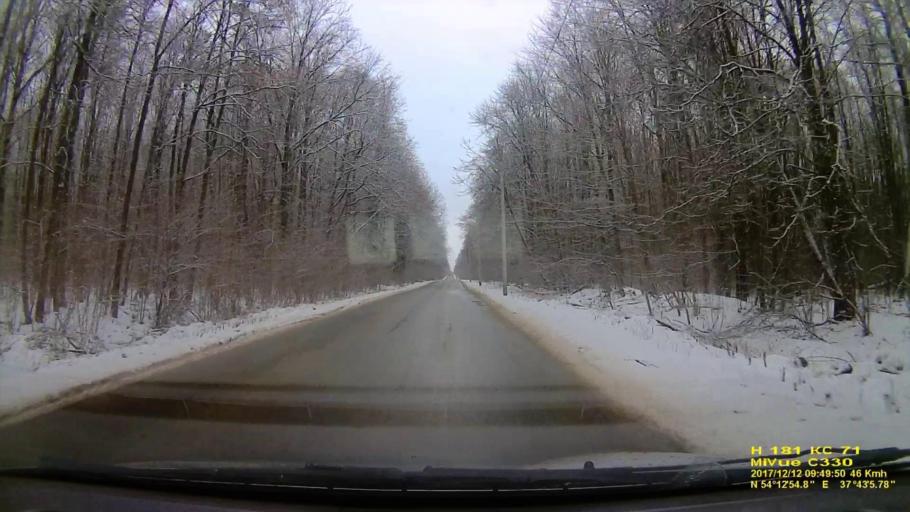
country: RU
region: Tula
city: Tula
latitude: 54.2152
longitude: 37.7187
